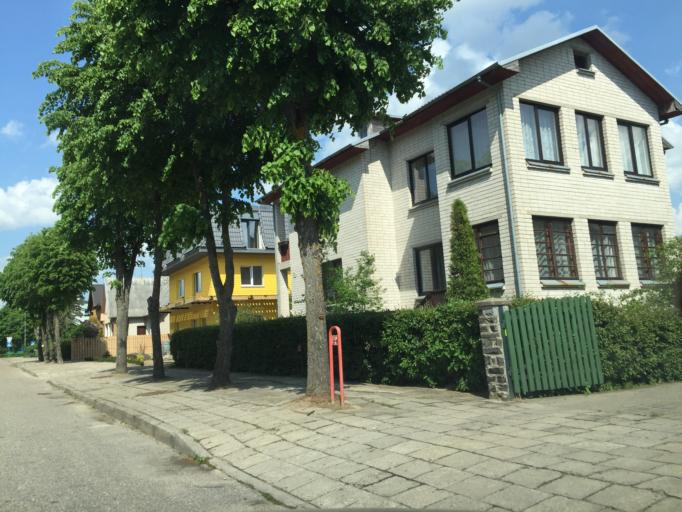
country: LT
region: Klaipedos apskritis
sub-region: Klaipeda
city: Palanga
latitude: 55.9255
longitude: 21.0627
